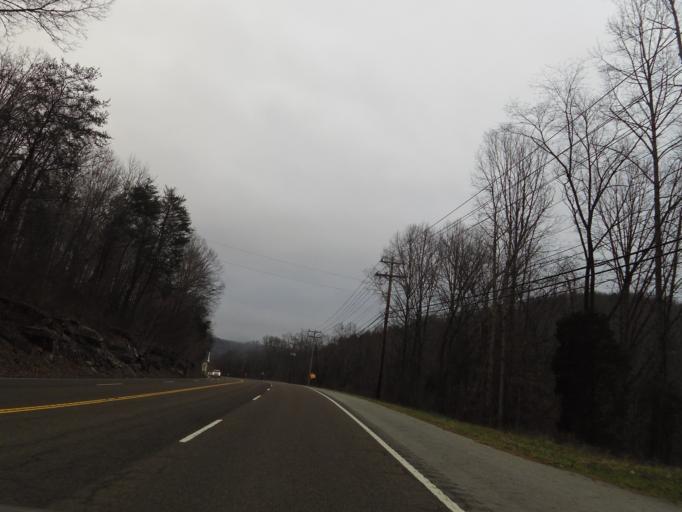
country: US
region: Tennessee
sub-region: Anderson County
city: Clinton
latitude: 36.0480
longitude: -84.1171
